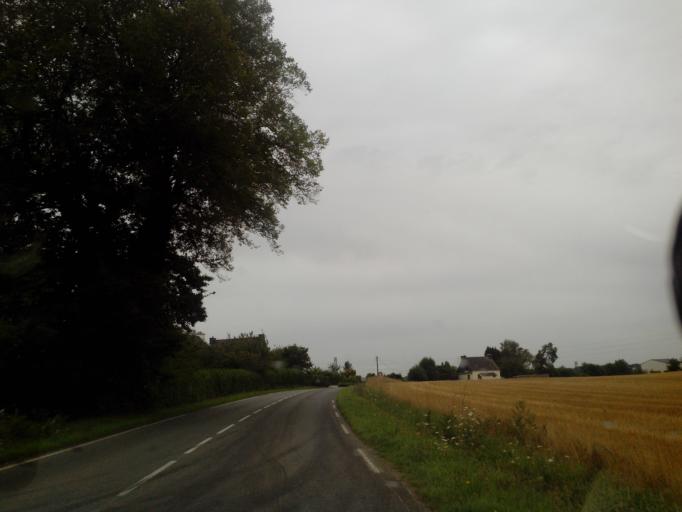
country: FR
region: Brittany
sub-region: Departement du Finistere
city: Tremeven
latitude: 47.8855
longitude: -3.5317
